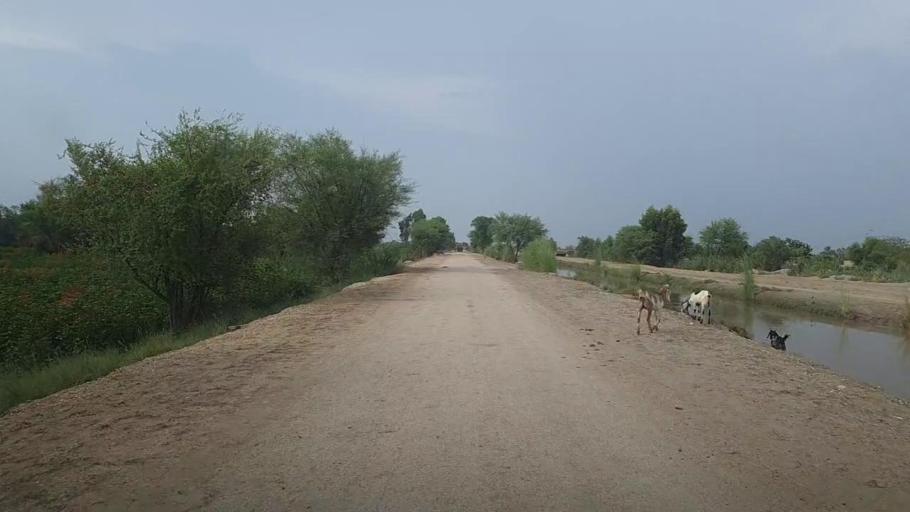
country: PK
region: Sindh
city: Karaundi
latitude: 26.9597
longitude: 68.4250
